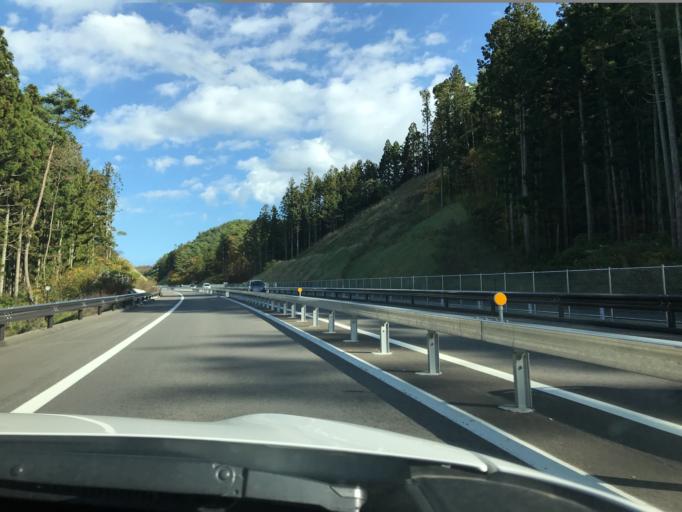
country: JP
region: Fukushima
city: Yanagawamachi-saiwaicho
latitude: 37.7543
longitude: 140.7096
